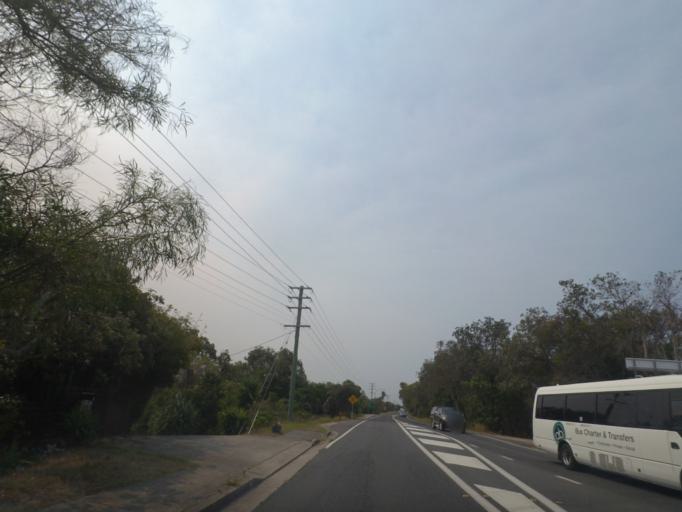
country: AU
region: New South Wales
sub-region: Tweed
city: Casuarina
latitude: -28.3286
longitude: 153.5686
